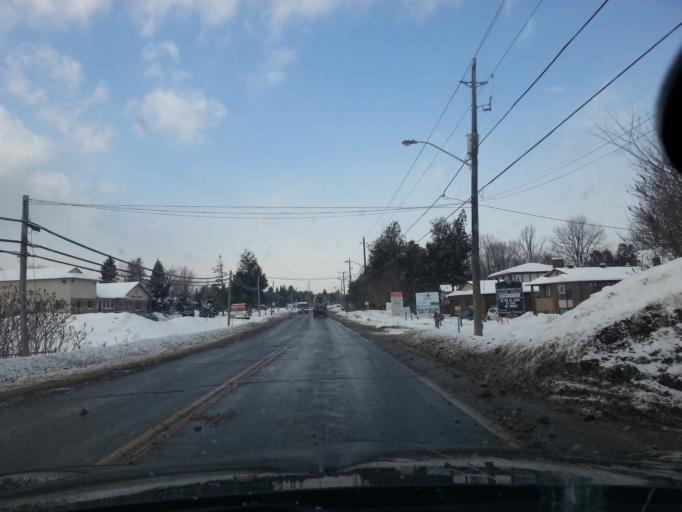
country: CA
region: Ontario
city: Bells Corners
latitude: 45.2706
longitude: -75.9432
